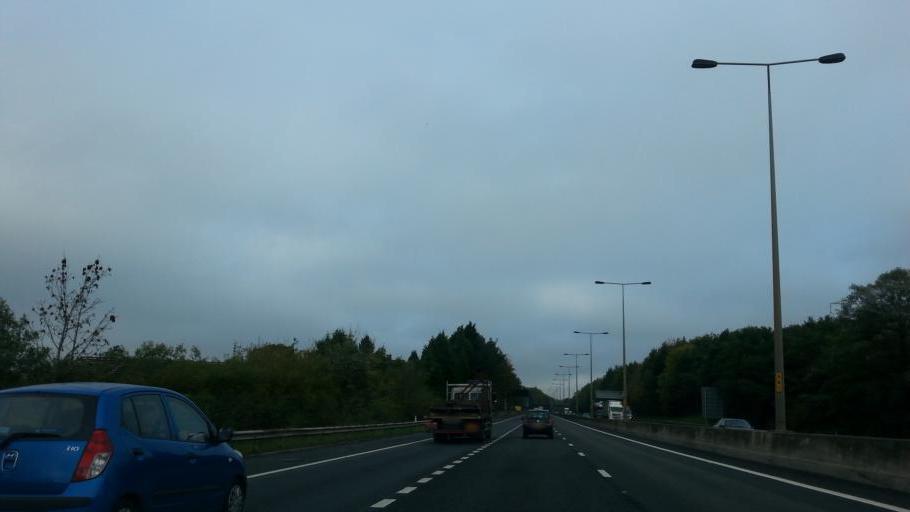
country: GB
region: England
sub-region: City and Borough of Birmingham
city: Bartley Green
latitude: 52.4376
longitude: -2.0178
